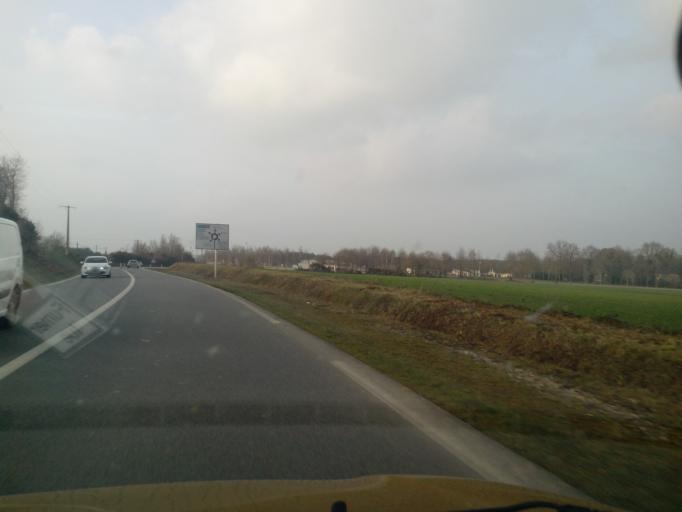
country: FR
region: Brittany
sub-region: Departement du Morbihan
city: Molac
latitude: 47.7756
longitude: -2.4533
